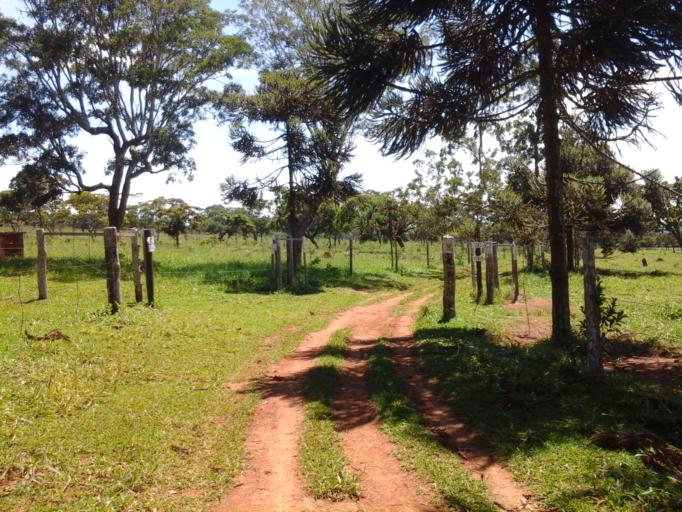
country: BR
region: Goias
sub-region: Abadiania
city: Abadiania
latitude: -15.9798
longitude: -48.5320
